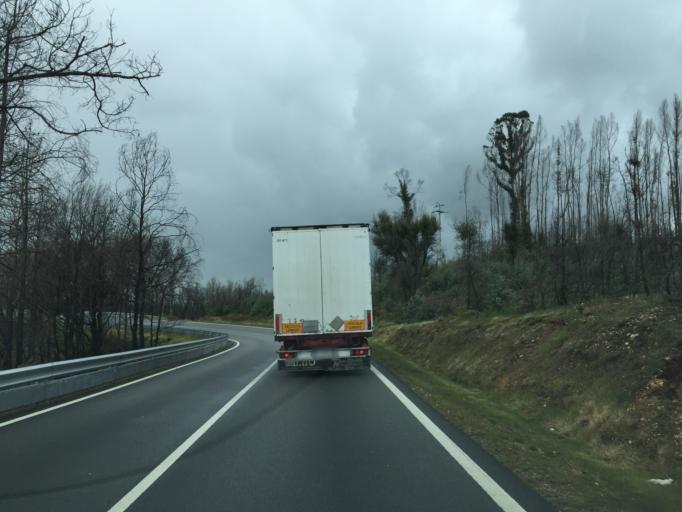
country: PT
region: Coimbra
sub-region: Oliveira do Hospital
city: Oliveira do Hospital
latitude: 40.3285
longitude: -7.9414
